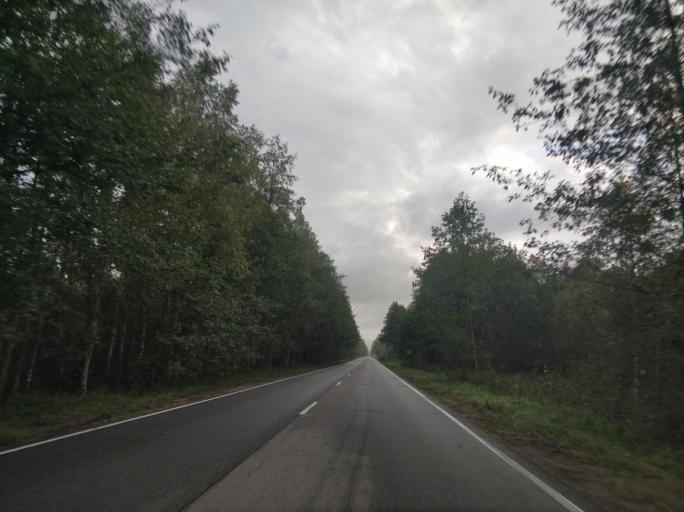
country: RU
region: Leningrad
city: Borisova Griva
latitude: 60.1412
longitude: 30.9508
